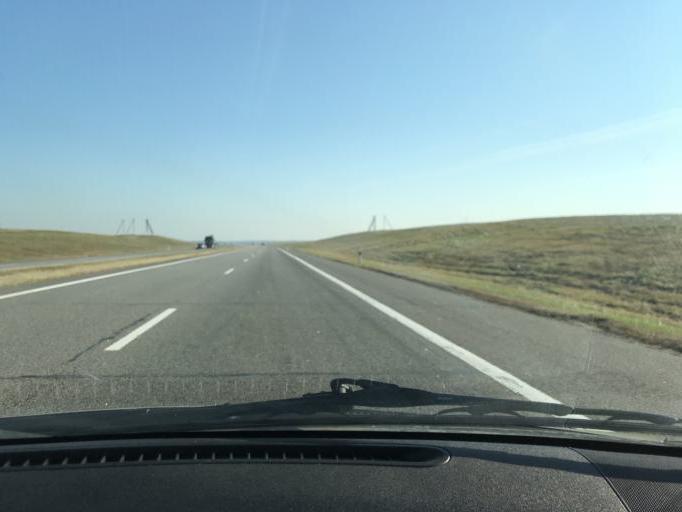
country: BY
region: Vitebsk
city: Talachyn
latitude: 54.4614
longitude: 29.7305
